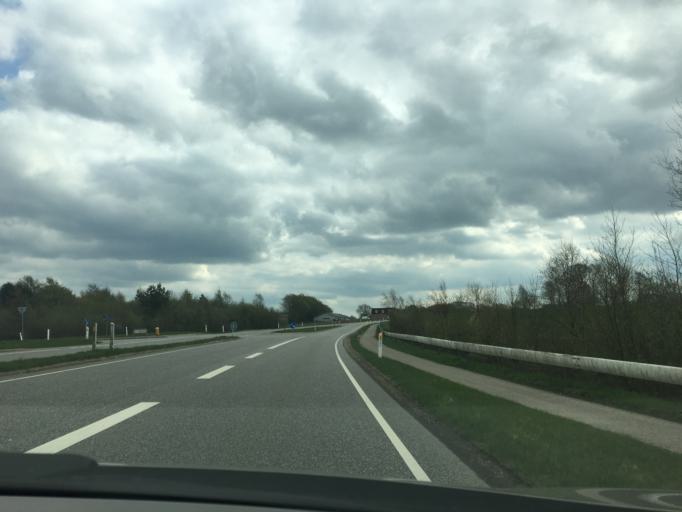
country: DK
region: Central Jutland
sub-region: Horsens Kommune
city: Braedstrup
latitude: 56.0340
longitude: 9.6104
